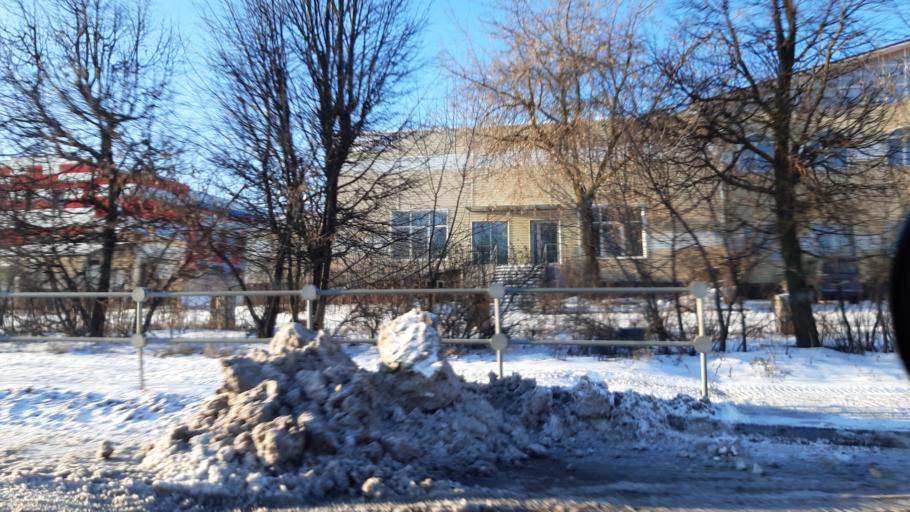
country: RU
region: Moskovskaya
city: Skoropuskovskiy
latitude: 56.3383
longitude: 38.1627
